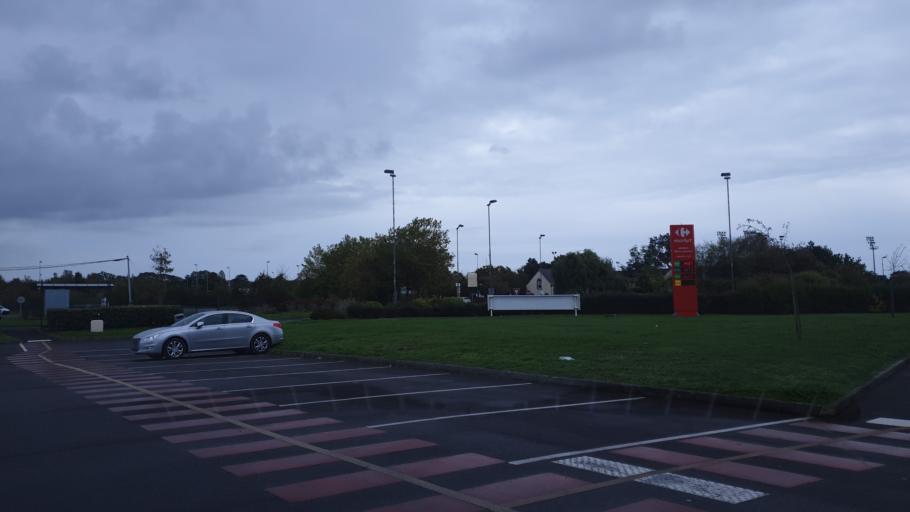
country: FR
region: Brittany
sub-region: Departement d'Ille-et-Vilaine
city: Chartres-de-Bretagne
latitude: 48.0464
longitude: -1.7109
